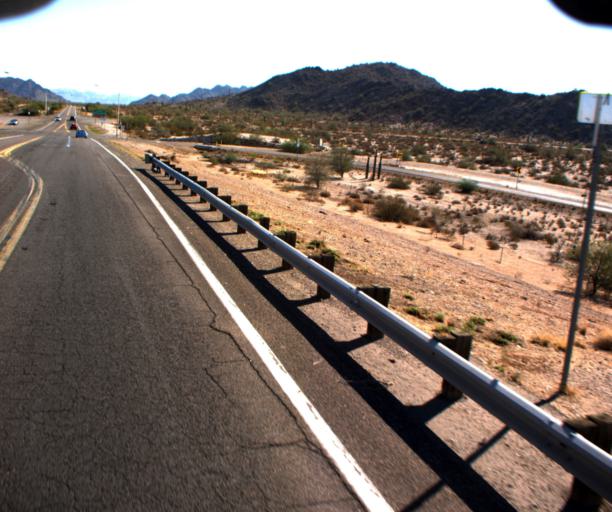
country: US
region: Arizona
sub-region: Pinal County
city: Sacaton
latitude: 33.0037
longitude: -111.7526
